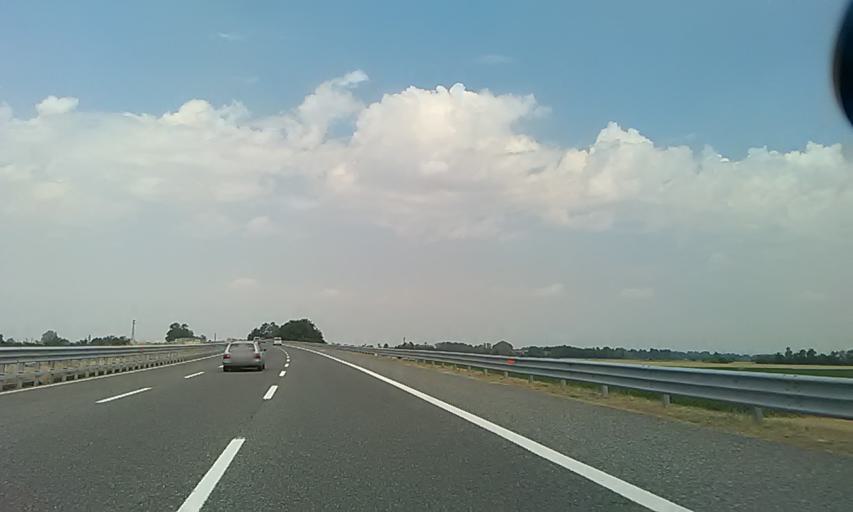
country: IT
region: Piedmont
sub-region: Provincia di Alessandria
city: Castellazzo Bormida
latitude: 44.8464
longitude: 8.5949
